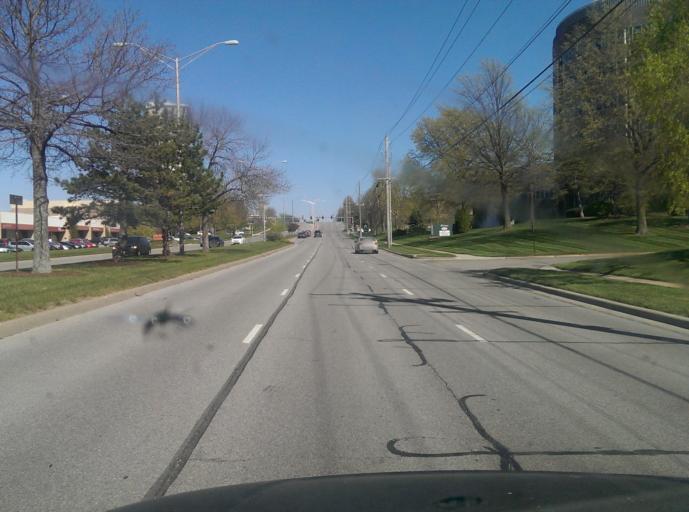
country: US
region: Kansas
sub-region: Johnson County
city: Overland Park
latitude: 38.9275
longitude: -94.6610
